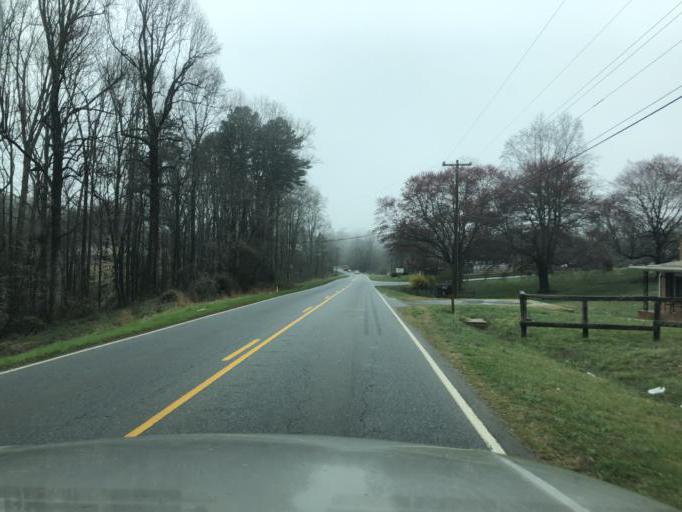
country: US
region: North Carolina
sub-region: Cleveland County
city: Shelby
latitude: 35.3288
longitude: -81.4690
